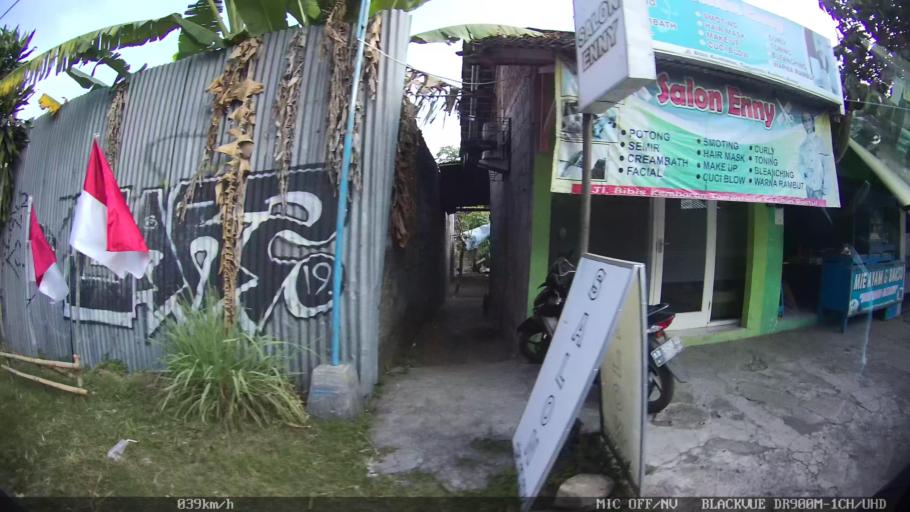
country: ID
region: Daerah Istimewa Yogyakarta
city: Kasihan
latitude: -7.8294
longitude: 110.3357
